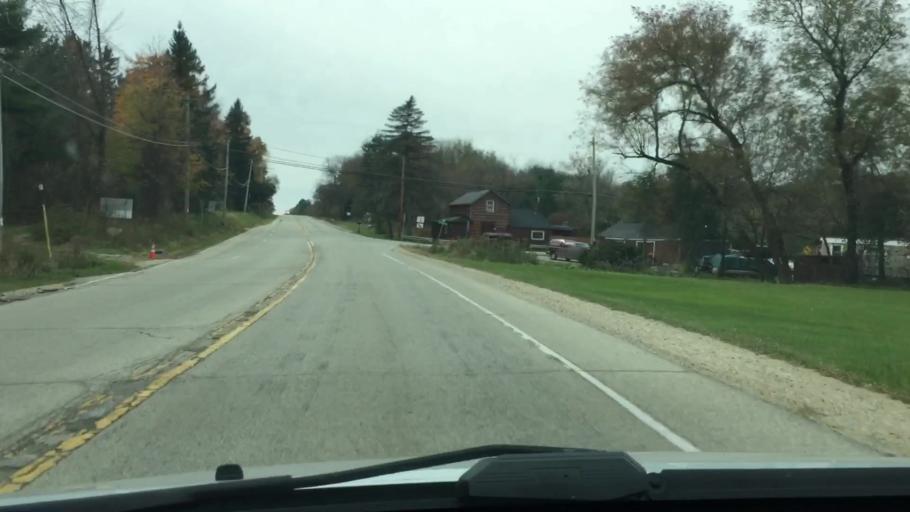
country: US
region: Wisconsin
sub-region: Waukesha County
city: New Berlin
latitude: 42.9587
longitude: -88.1376
